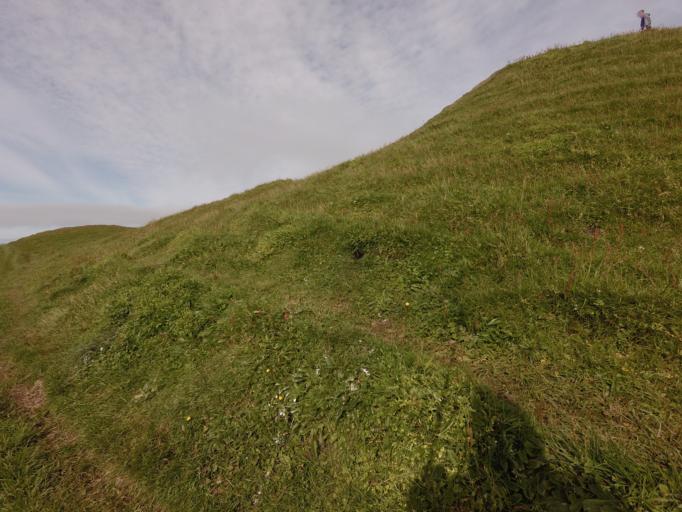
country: FO
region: Vagar
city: Sorvagur
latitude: 62.1029
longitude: -7.6576
